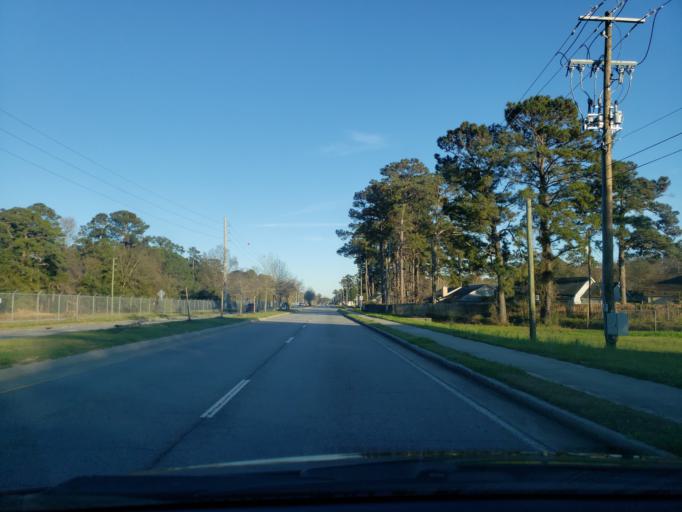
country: US
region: Georgia
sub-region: Chatham County
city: Montgomery
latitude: 32.0027
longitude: -81.1415
